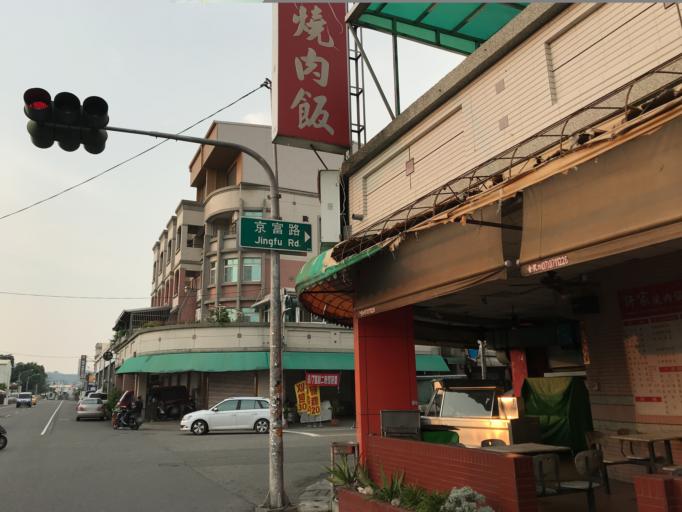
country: TW
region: Taiwan
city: Fengshan
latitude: 22.6774
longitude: 120.3311
